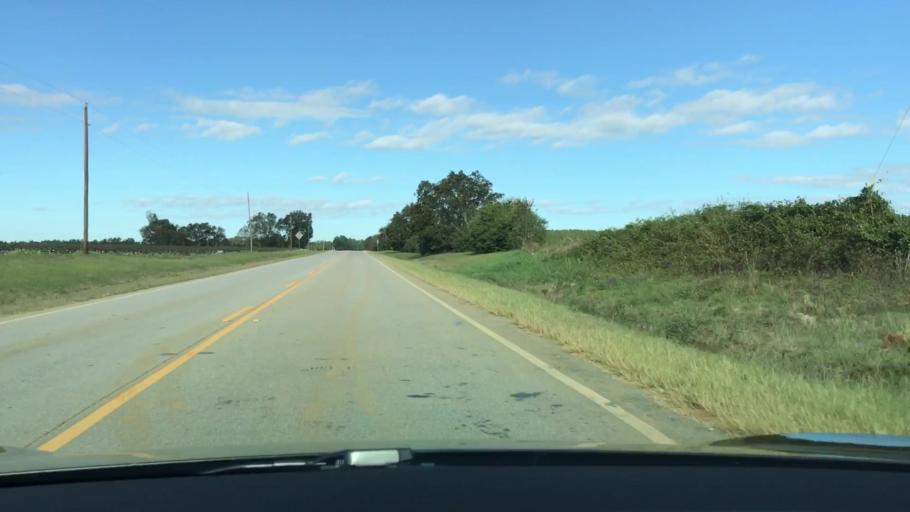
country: US
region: Georgia
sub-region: Jefferson County
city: Wrens
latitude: 33.1965
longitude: -82.4624
